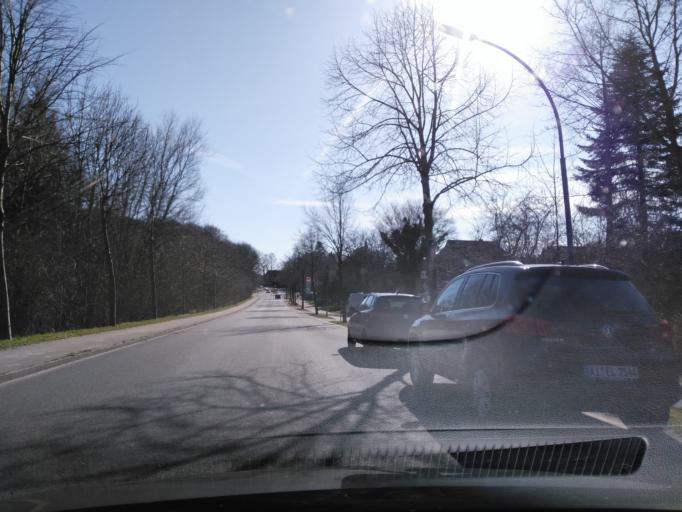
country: DE
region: Schleswig-Holstein
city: Molfsee
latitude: 54.2834
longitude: 10.0820
